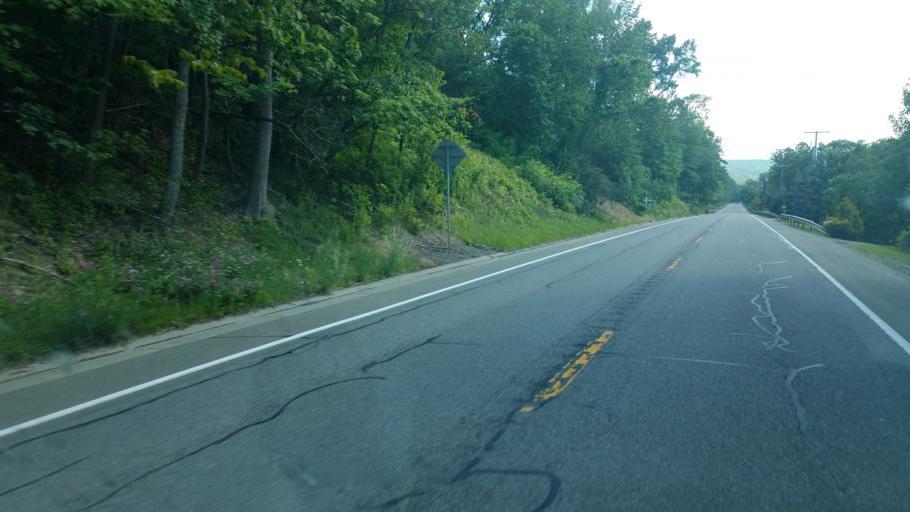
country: US
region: New York
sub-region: Steuben County
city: Sylvan Beach
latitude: 42.4380
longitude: -77.1728
